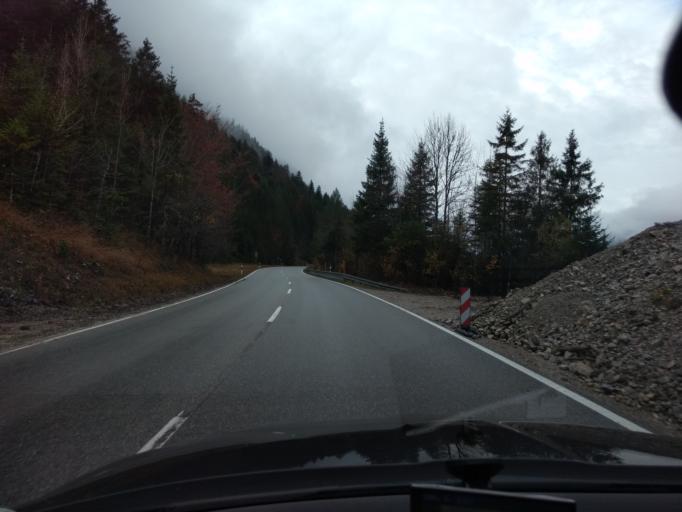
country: DE
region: Bavaria
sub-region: Upper Bavaria
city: Jachenau
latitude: 47.5602
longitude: 11.5003
